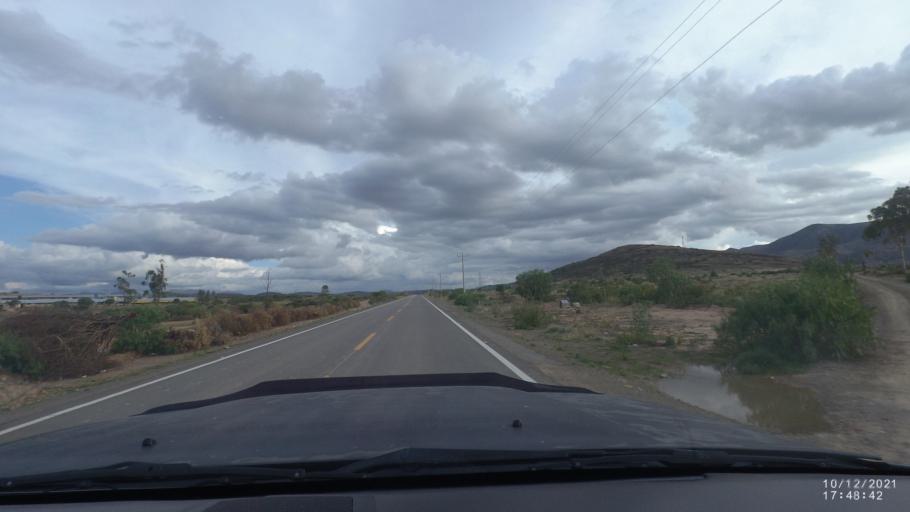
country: BO
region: Cochabamba
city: Tarata
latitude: -17.6484
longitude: -65.9762
